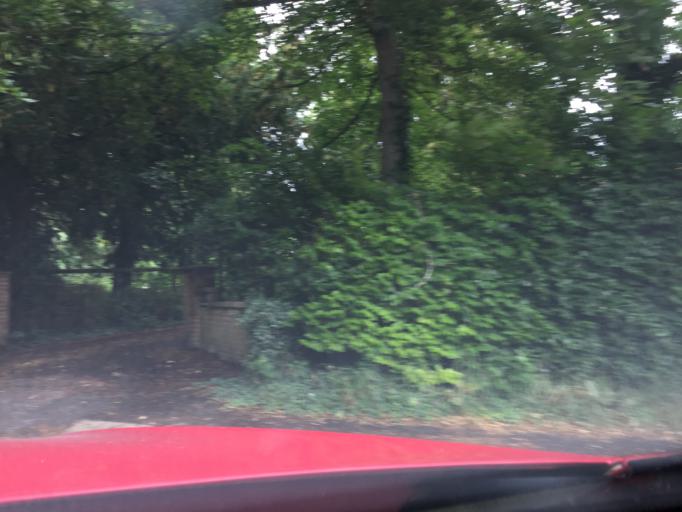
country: GB
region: England
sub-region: Warwickshire
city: Southam
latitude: 52.2261
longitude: -1.3913
